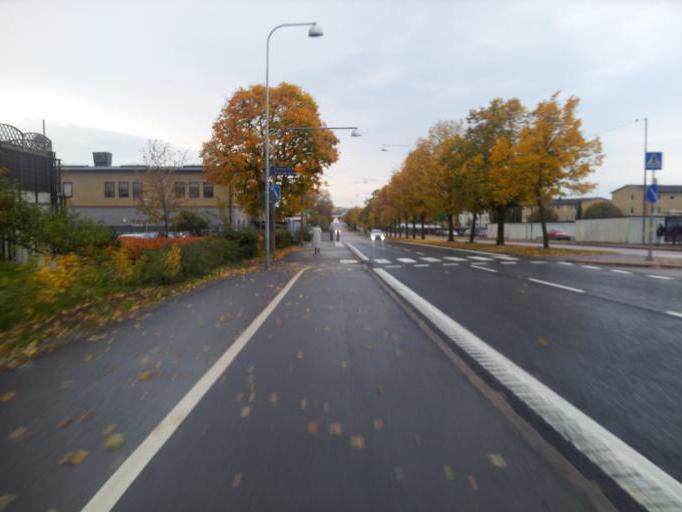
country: SE
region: Uppsala
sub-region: Uppsala Kommun
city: Uppsala
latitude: 59.8723
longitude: 17.6684
